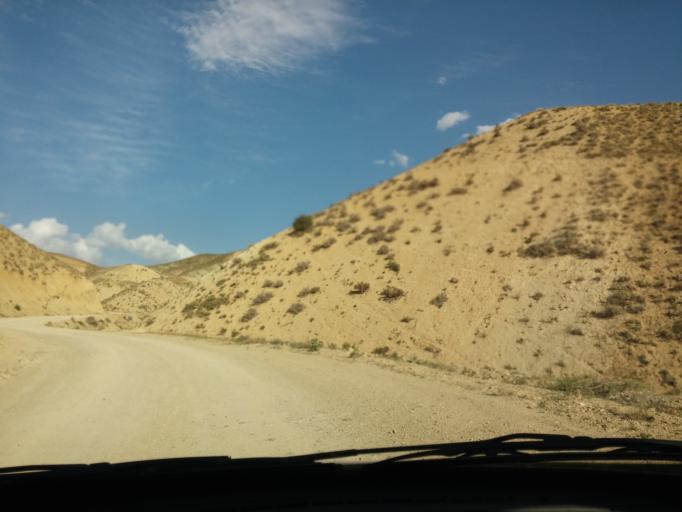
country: IR
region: Tehran
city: Damavand
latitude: 35.5352
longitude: 52.1973
